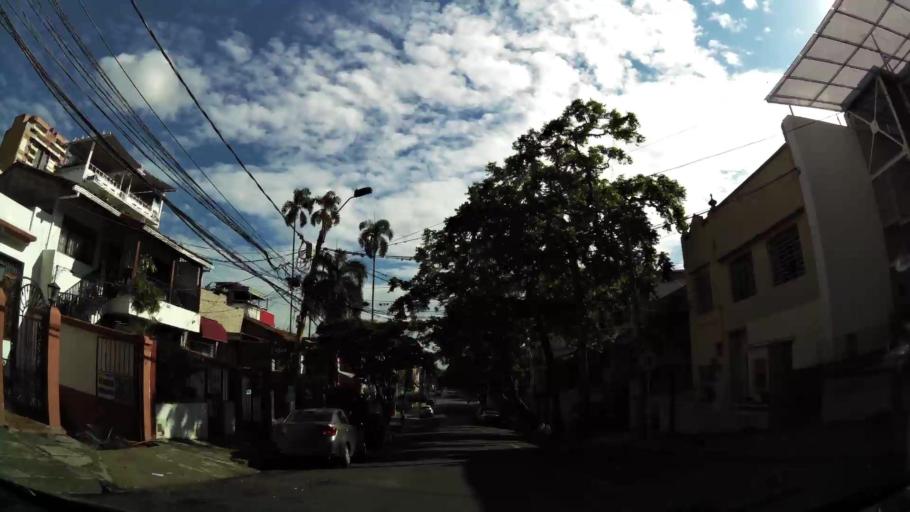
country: CO
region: Valle del Cauca
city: Cali
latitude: 3.4567
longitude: -76.5363
